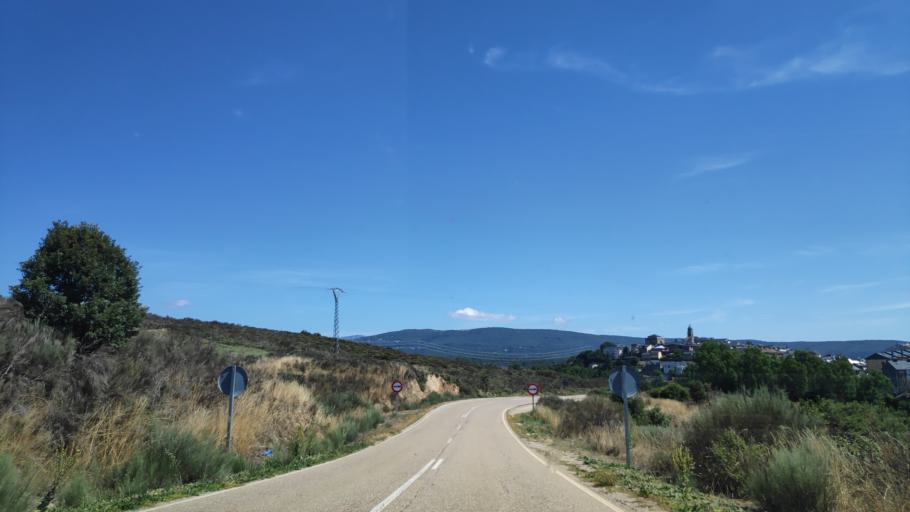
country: ES
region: Castille and Leon
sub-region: Provincia de Zamora
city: Puebla de Sanabria
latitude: 42.0503
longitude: -6.6420
